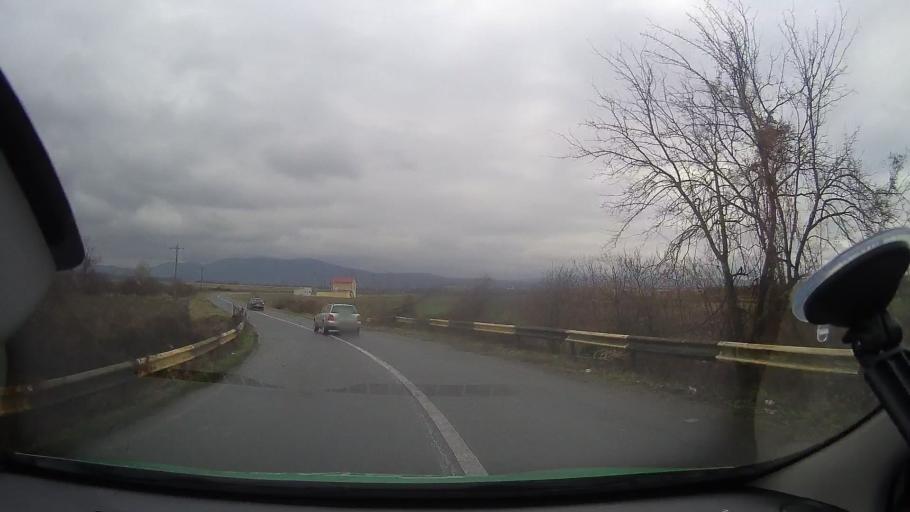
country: RO
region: Arad
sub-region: Comuna Sebis
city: Sebis
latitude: 46.3487
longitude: 22.1287
